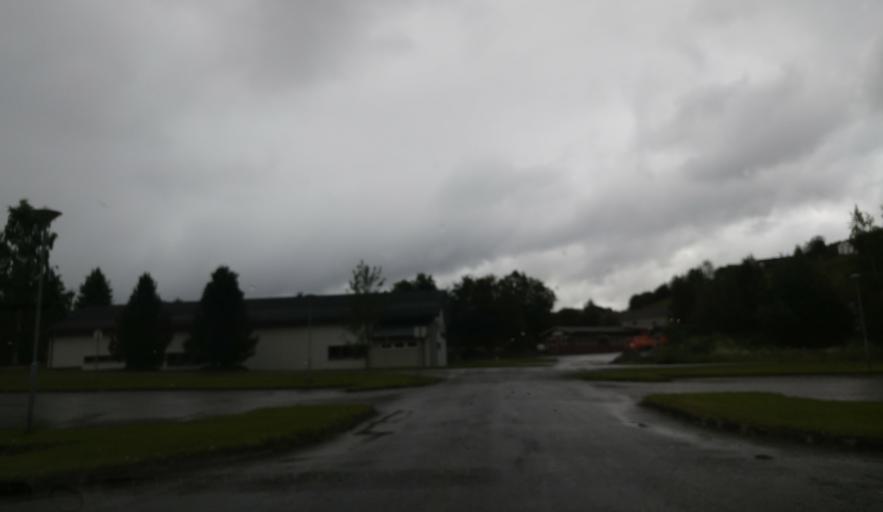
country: NO
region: Sor-Trondelag
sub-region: Selbu
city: Mebonden
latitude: 63.2167
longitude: 11.0411
